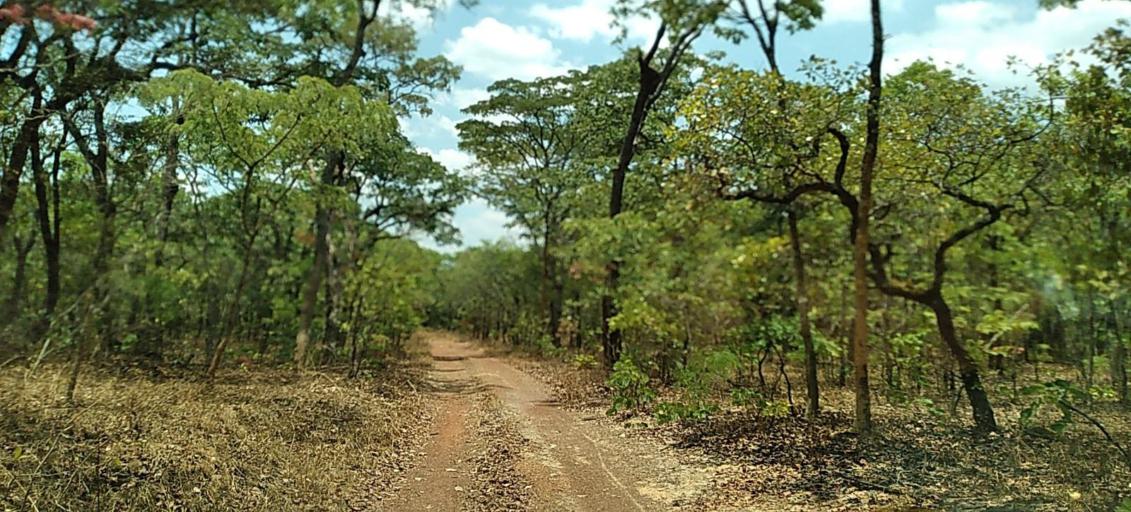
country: ZM
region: Copperbelt
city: Chililabombwe
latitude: -12.4557
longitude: 27.6979
